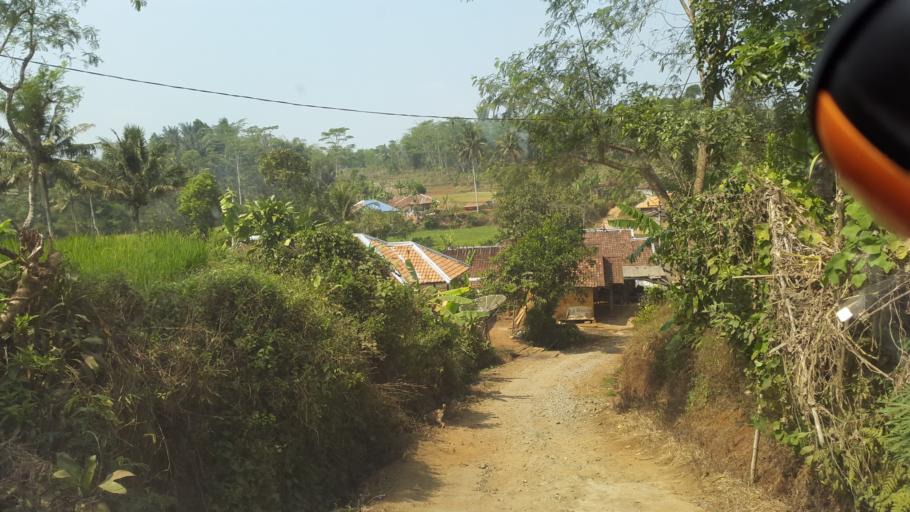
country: ID
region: West Java
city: Sukajaya
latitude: -7.2184
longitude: 106.7603
